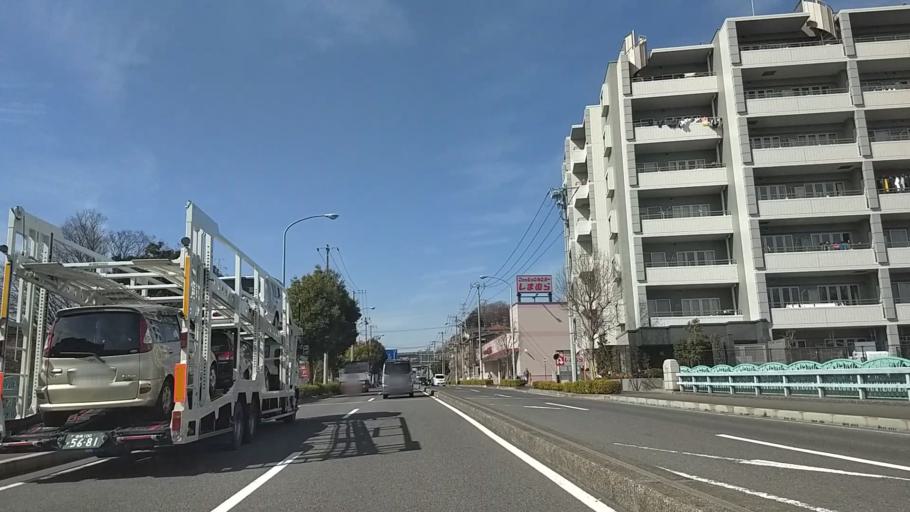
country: JP
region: Kanagawa
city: Kamakura
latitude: 35.3786
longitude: 139.5533
